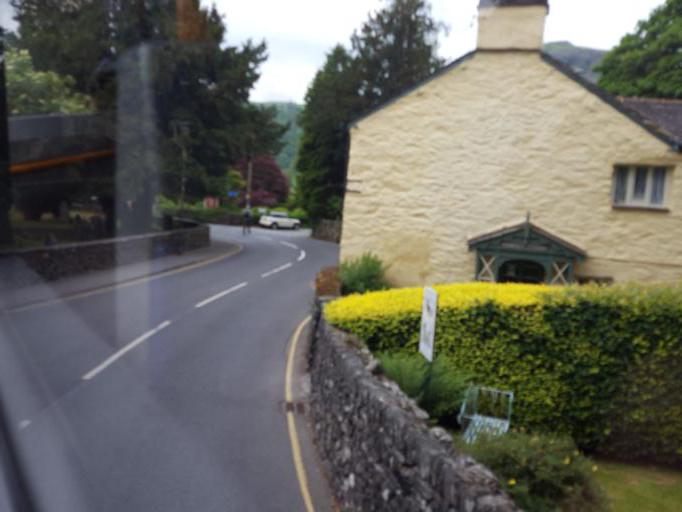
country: GB
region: England
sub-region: Cumbria
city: Ambleside
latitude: 54.4582
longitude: -3.0237
